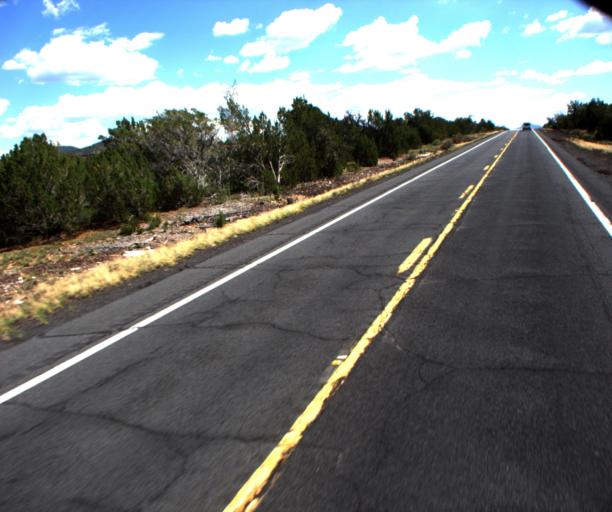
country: US
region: Arizona
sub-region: Coconino County
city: Williams
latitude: 35.4525
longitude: -112.1708
